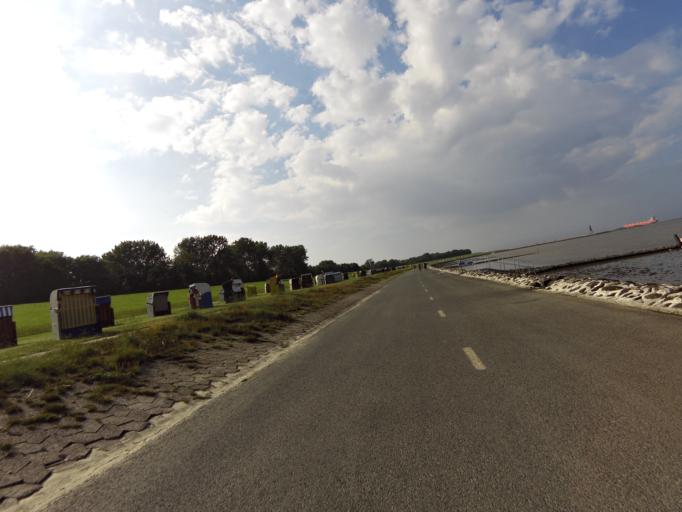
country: DE
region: Lower Saxony
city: Cuxhaven
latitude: 53.8820
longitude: 8.6848
